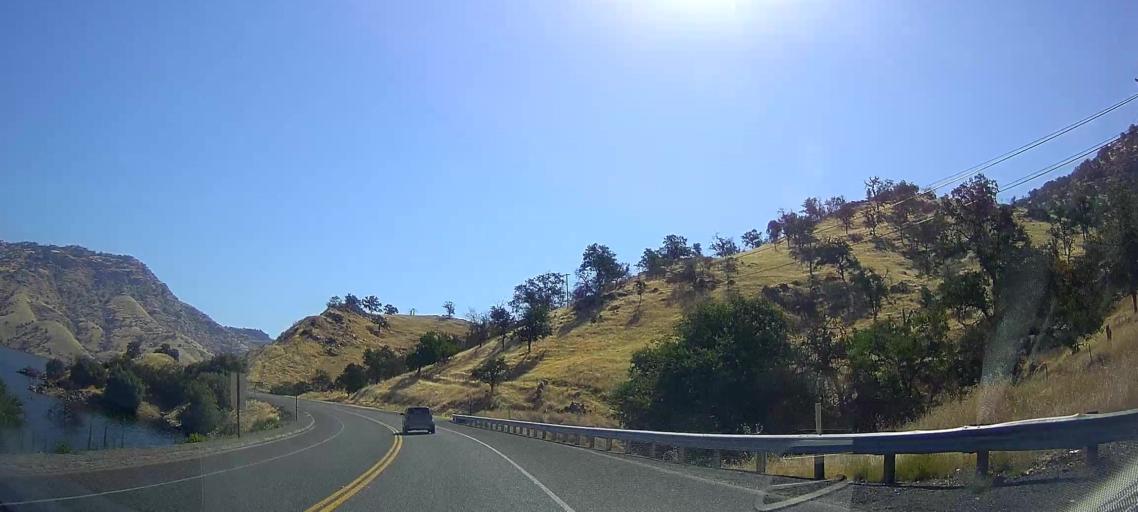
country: US
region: California
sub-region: Tulare County
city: Three Rivers
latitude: 36.3961
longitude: -118.9876
